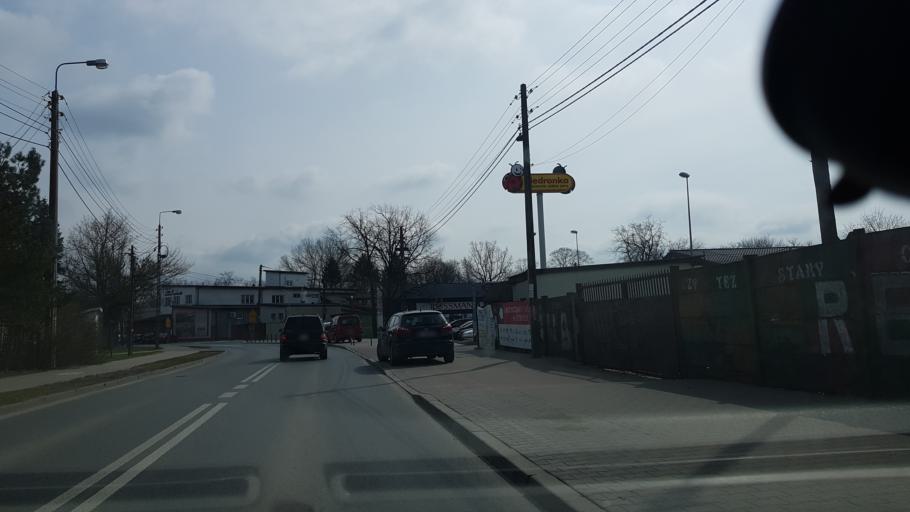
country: PL
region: Masovian Voivodeship
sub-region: Warszawa
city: Rembertow
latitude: 52.2594
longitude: 21.1553
